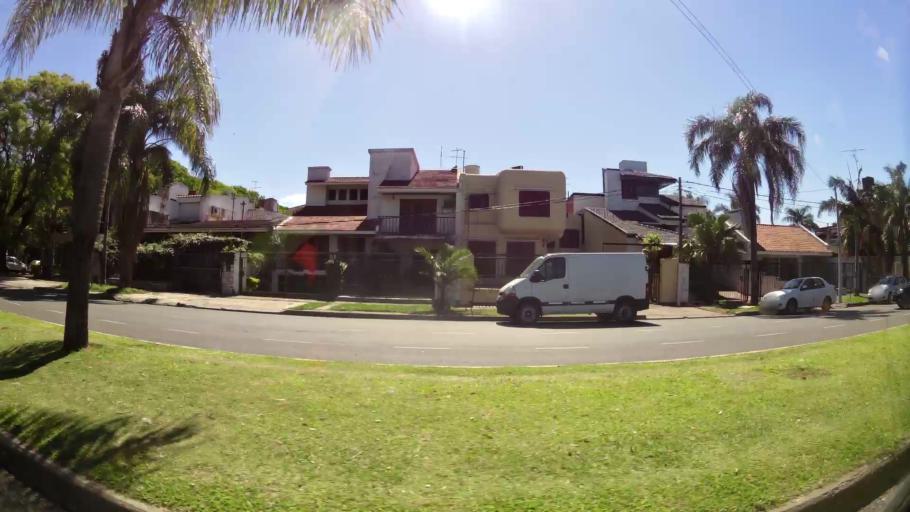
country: AR
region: Santa Fe
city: Santa Fe de la Vera Cruz
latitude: -31.6228
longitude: -60.6786
